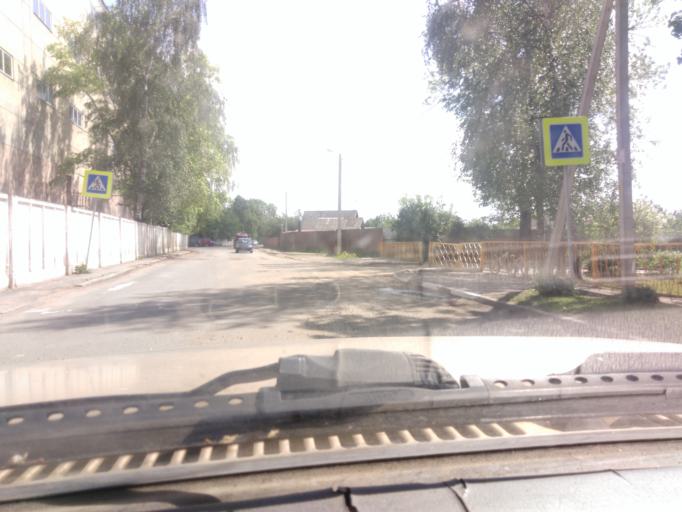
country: BY
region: Mogilev
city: Mahilyow
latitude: 53.9260
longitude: 30.3336
